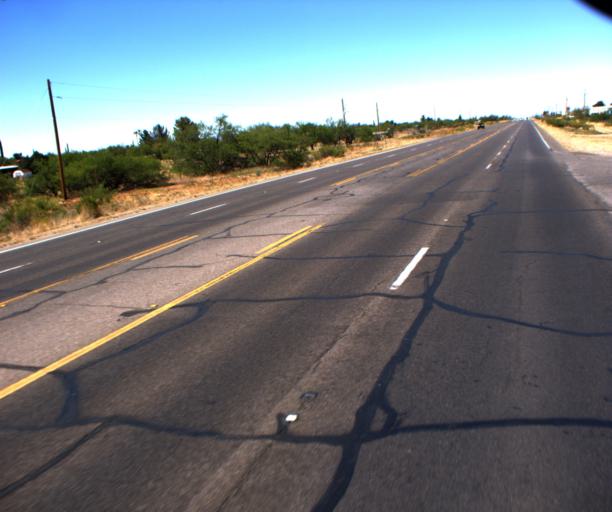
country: US
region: Arizona
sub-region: Cochise County
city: Sierra Vista Southeast
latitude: 31.4707
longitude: -110.2573
